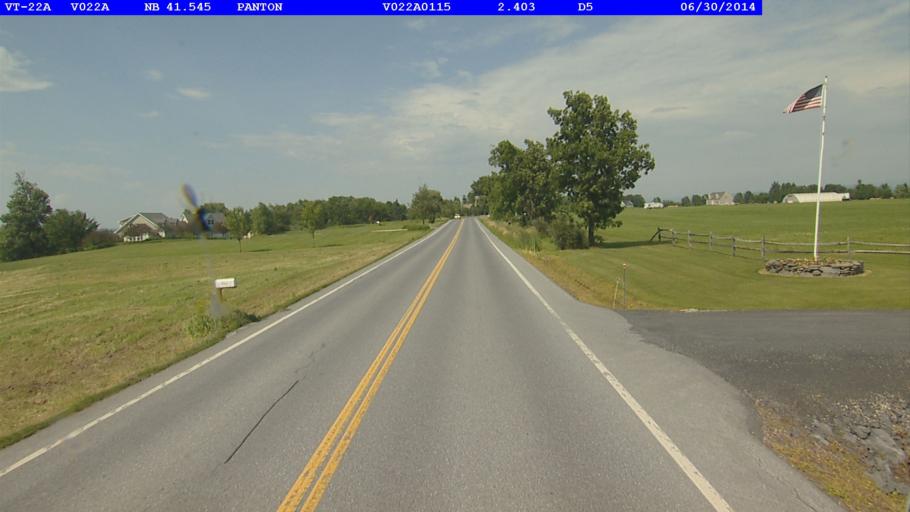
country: US
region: Vermont
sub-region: Addison County
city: Vergennes
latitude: 44.1507
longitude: -73.2725
